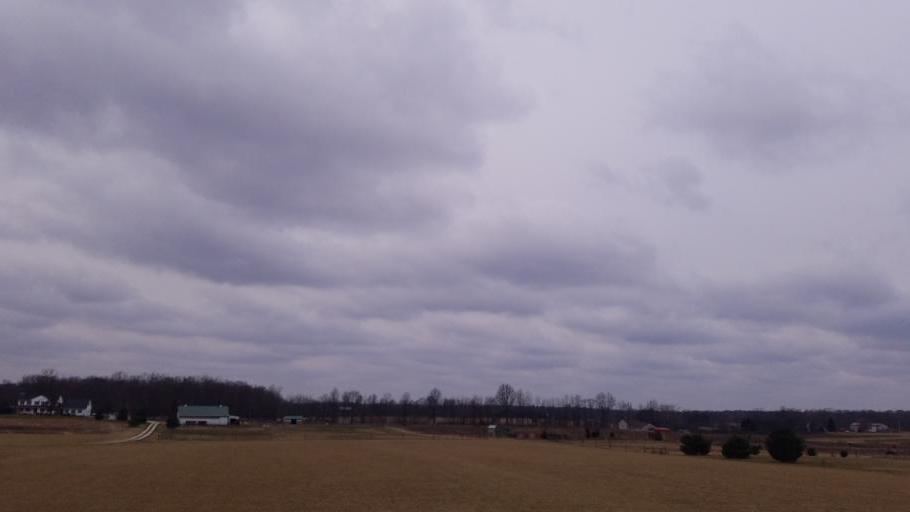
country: US
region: Ohio
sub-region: Crawford County
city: Crestline
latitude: 40.7295
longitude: -82.7032
